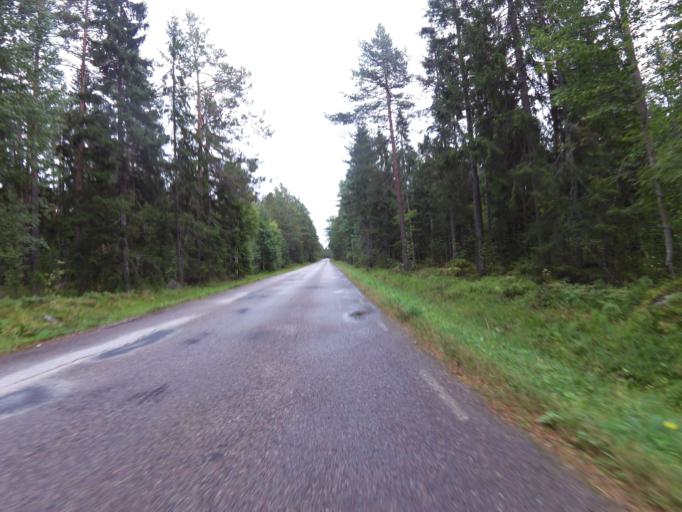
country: SE
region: Gaevleborg
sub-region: Gavle Kommun
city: Valbo
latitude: 60.6692
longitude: 16.9168
